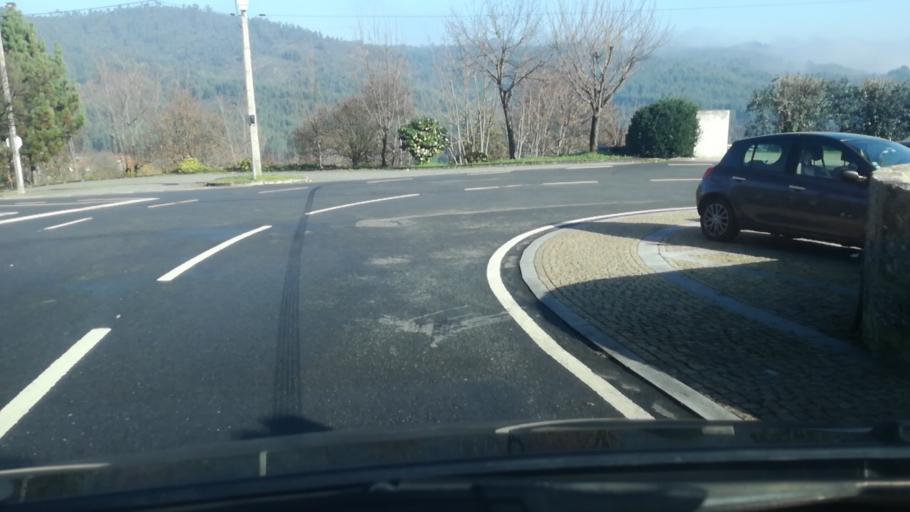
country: PT
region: Braga
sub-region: Guimaraes
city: Ponte
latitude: 41.5277
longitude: -8.3410
